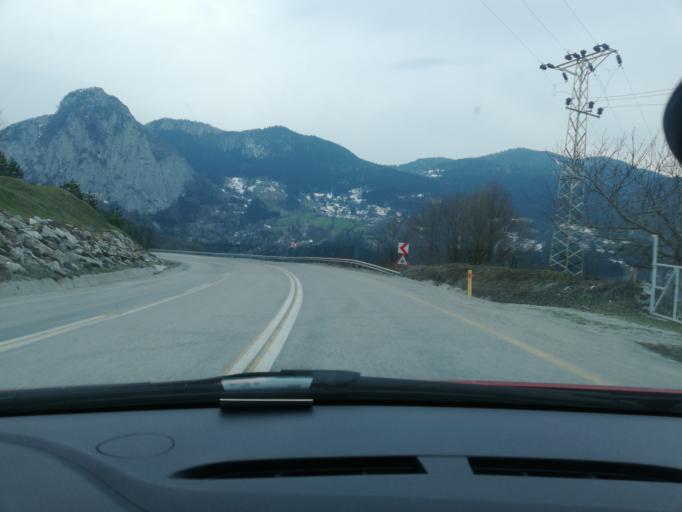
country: TR
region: Kastamonu
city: Kure
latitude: 41.8478
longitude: 33.7216
